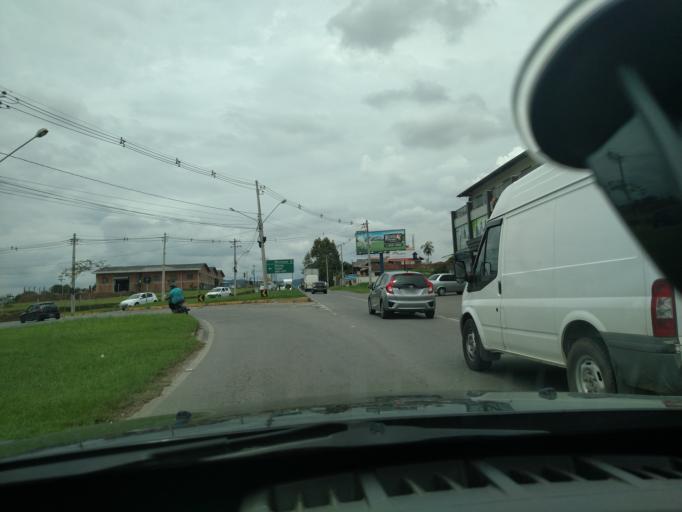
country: BR
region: Santa Catarina
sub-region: Gaspar
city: Gaspar
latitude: -26.9319
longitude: -48.9457
